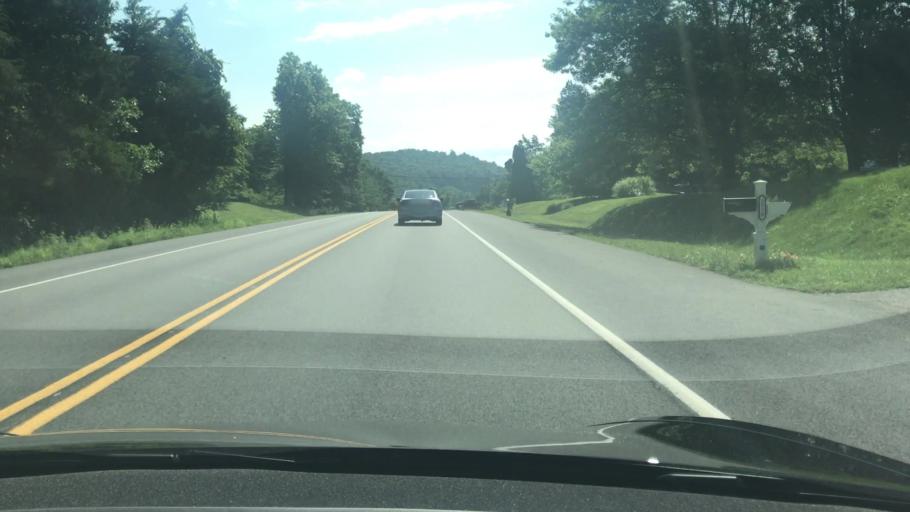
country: US
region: Pennsylvania
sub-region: York County
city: Valley Green
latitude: 40.1311
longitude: -76.8233
